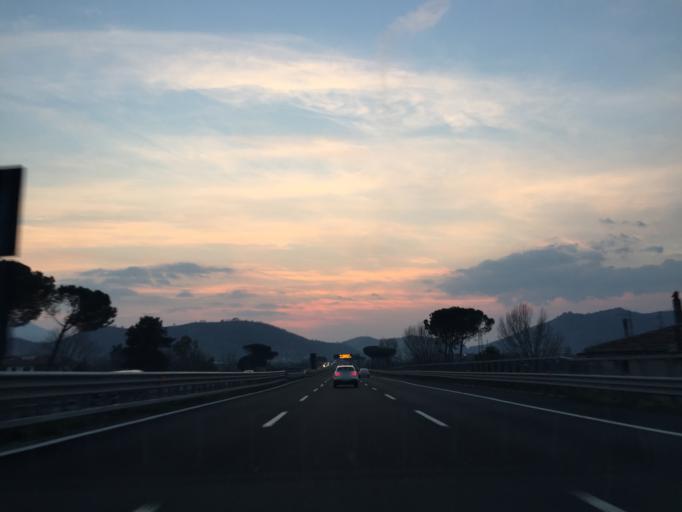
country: IT
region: Campania
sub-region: Provincia di Salerno
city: Roccapiemonte
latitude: 40.7676
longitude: 14.6966
